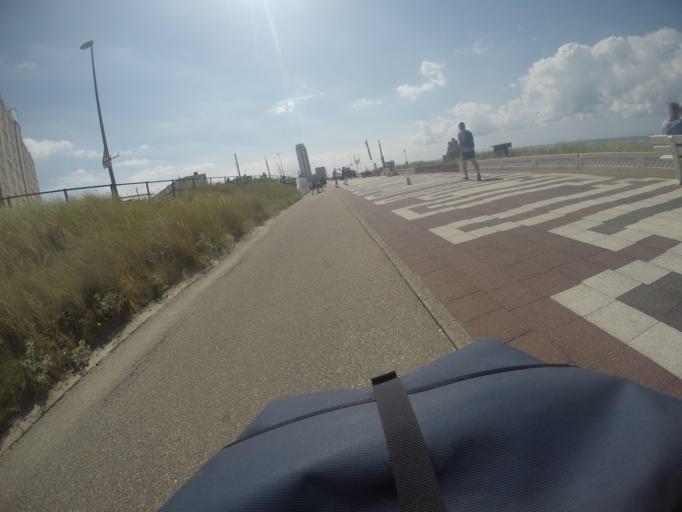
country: NL
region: North Holland
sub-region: Gemeente Zandvoort
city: Zandvoort
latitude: 52.3817
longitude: 4.5295
